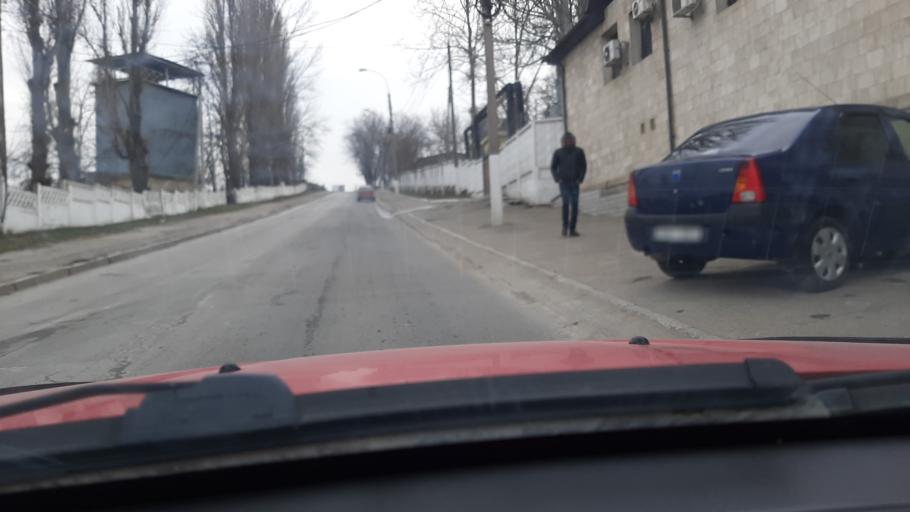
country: MD
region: Chisinau
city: Vatra
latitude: 47.0379
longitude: 28.7942
